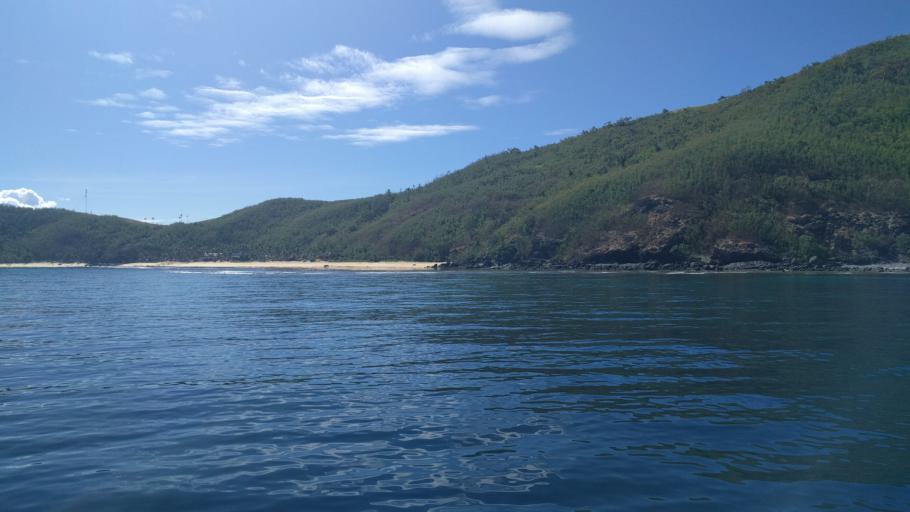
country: FJ
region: Western
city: Lautoka
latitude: -17.2811
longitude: 177.1032
